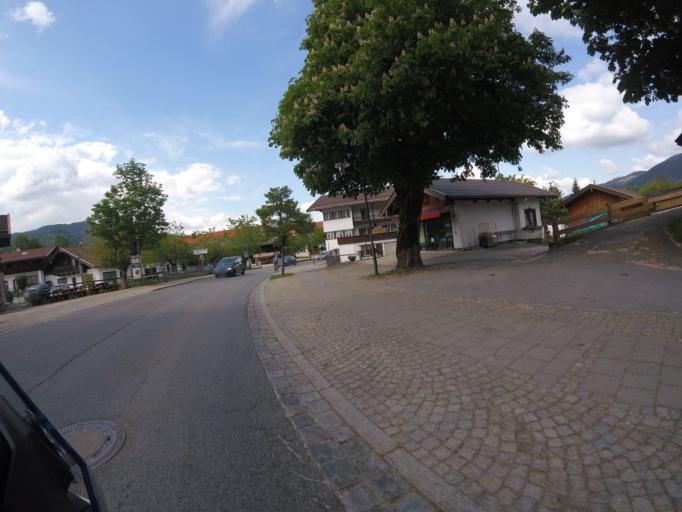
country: DE
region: Bavaria
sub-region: Upper Bavaria
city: Bad Wiessee
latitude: 47.7114
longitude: 11.7254
